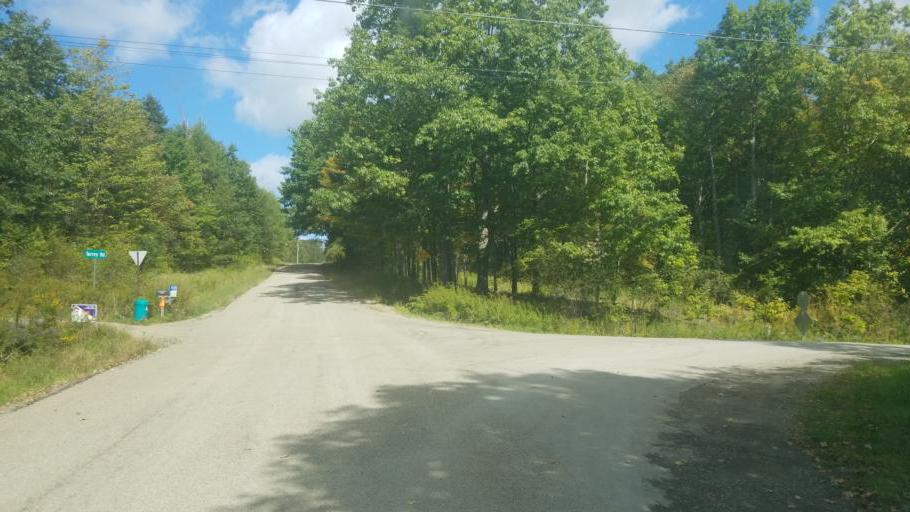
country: US
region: New York
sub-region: Allegany County
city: Cuba
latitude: 42.1978
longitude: -78.3090
